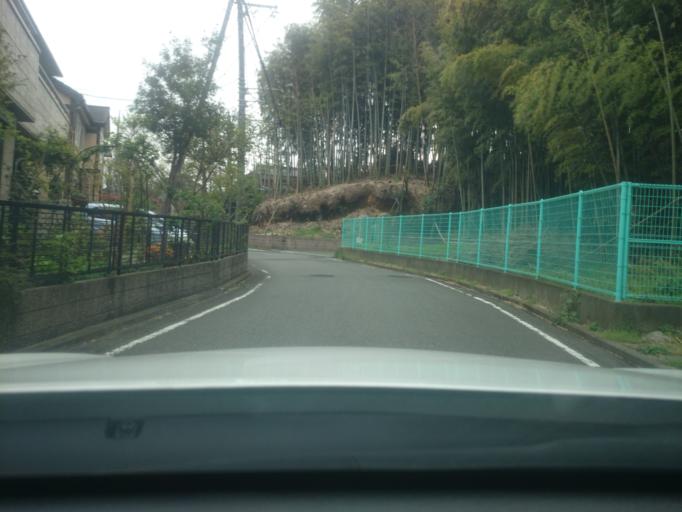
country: JP
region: Tokyo
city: Chofugaoka
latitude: 35.5669
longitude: 139.5739
